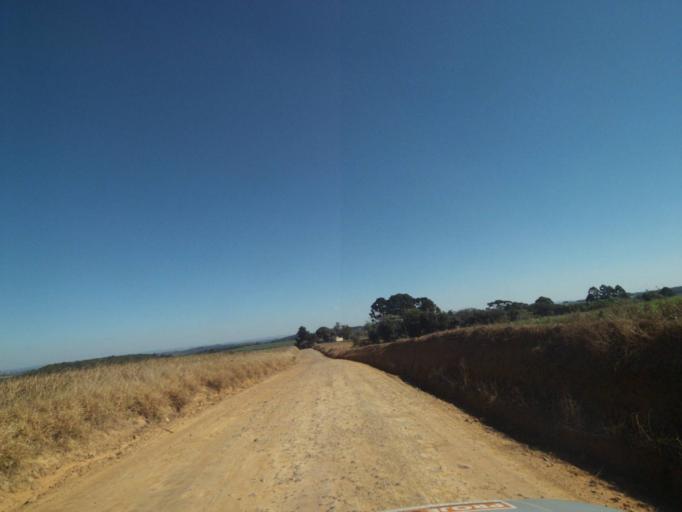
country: BR
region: Parana
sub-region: Tibagi
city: Tibagi
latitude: -24.6198
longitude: -50.6117
